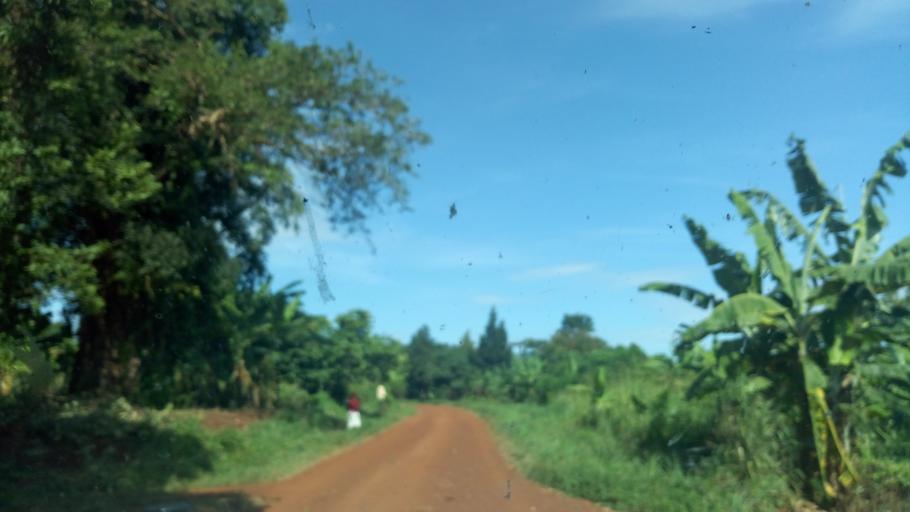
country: UG
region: Western Region
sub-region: Masindi District
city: Masindi
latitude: 1.6409
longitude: 31.7577
